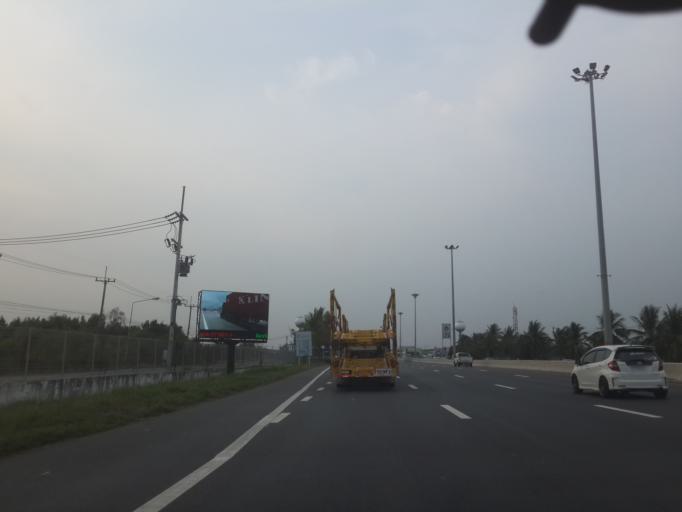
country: TH
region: Chachoengsao
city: Bang Pakong
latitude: 13.5344
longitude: 101.0128
